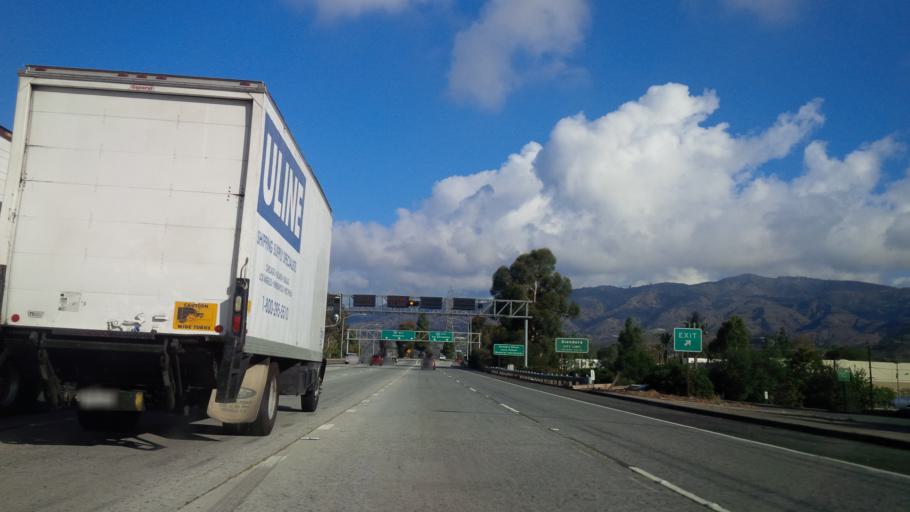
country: US
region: California
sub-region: Los Angeles County
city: San Dimas
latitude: 34.1150
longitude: -117.8239
